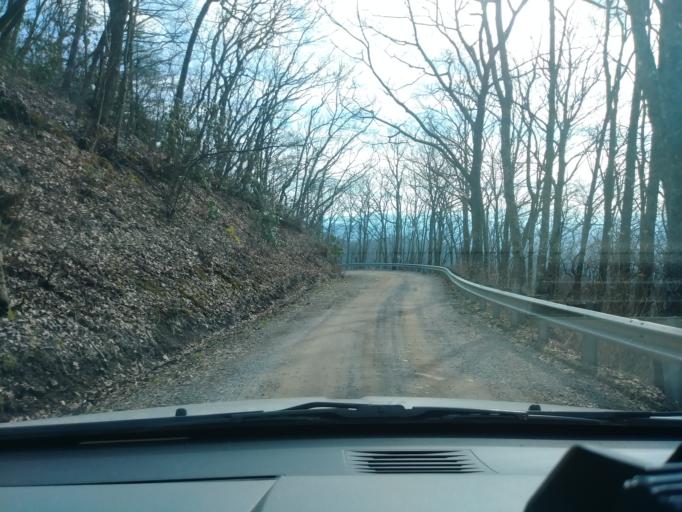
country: US
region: Tennessee
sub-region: Greene County
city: Tusculum
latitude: 36.0297
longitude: -82.7191
